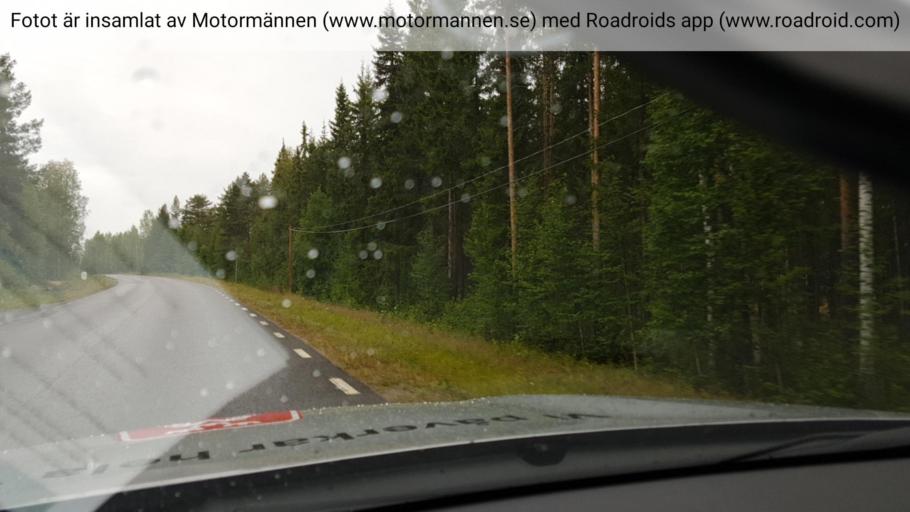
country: SE
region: Norrbotten
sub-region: Bodens Kommun
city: Boden
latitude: 65.8789
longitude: 21.3772
